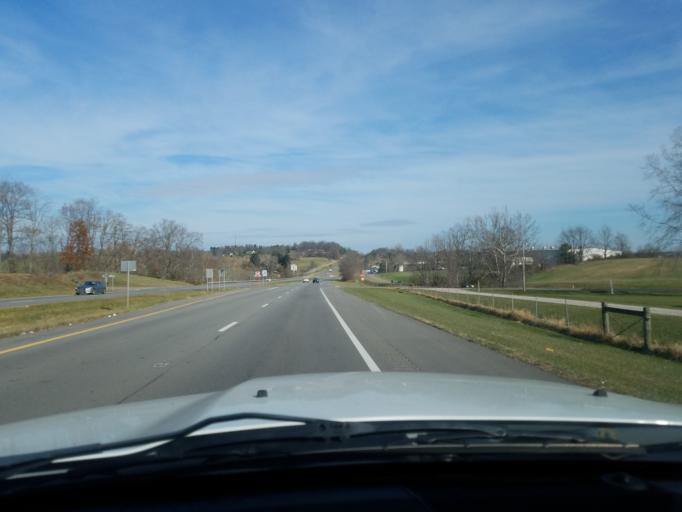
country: US
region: Ohio
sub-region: Athens County
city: Athens
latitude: 39.2483
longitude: -82.1813
